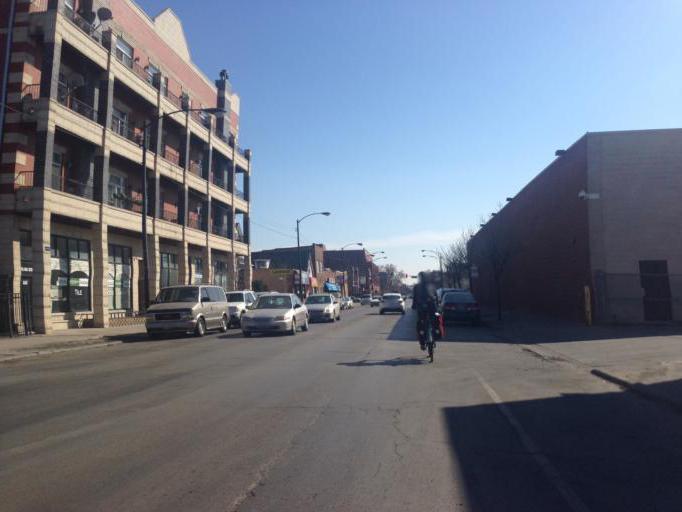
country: US
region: Illinois
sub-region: Cook County
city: Lincolnwood
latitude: 41.9590
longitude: -87.7082
